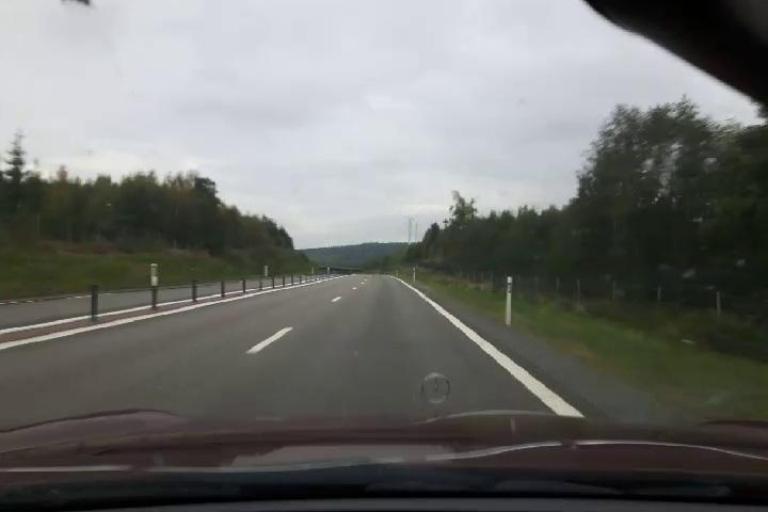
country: SE
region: Vaesternorrland
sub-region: Haernoesands Kommun
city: Haernoesand
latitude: 62.7613
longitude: 17.9053
